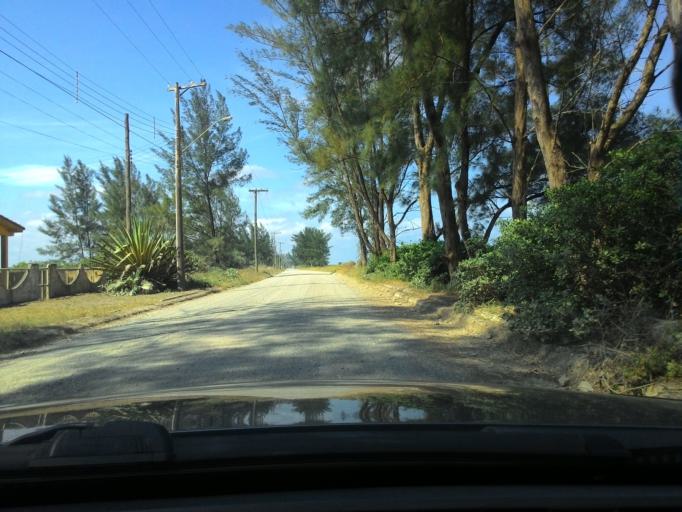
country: BR
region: Sao Paulo
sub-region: Iguape
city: Iguape
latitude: -24.8419
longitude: -47.6832
